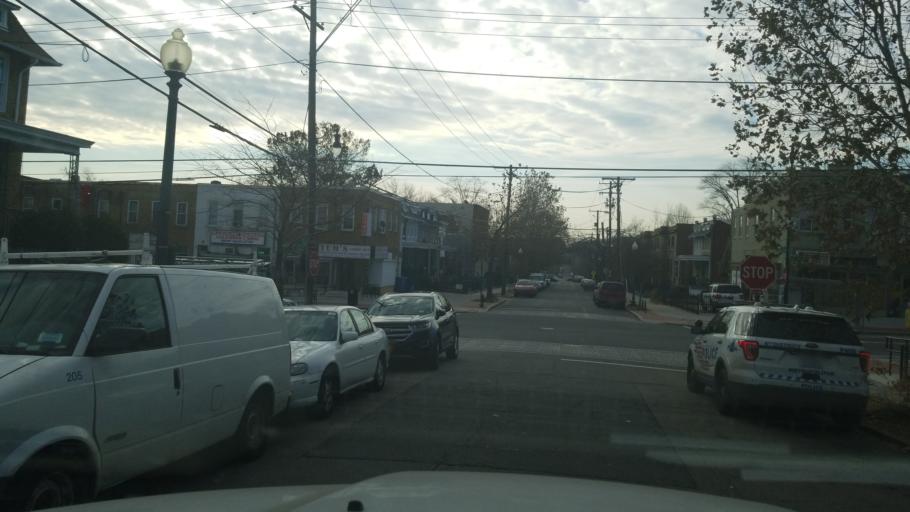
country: US
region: Maryland
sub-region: Montgomery County
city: Takoma Park
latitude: 38.9567
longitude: -77.0224
